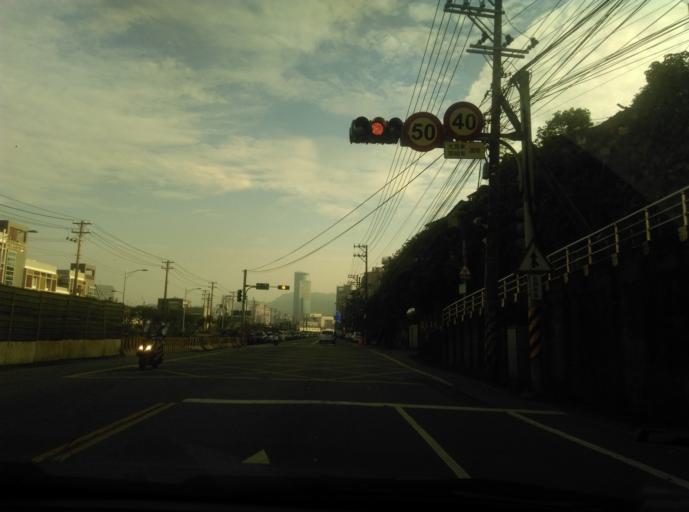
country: TW
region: Taiwan
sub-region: Keelung
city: Keelung
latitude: 25.1416
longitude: 121.7387
